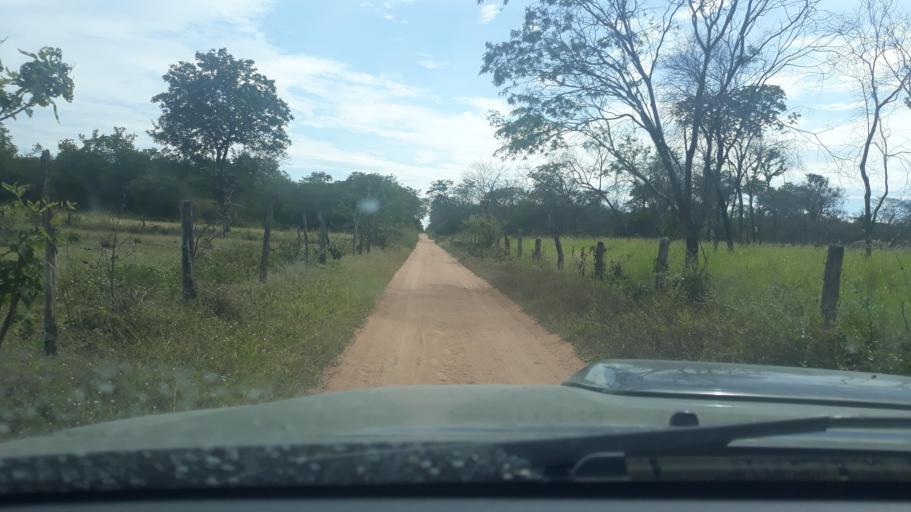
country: BR
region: Bahia
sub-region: Riacho De Santana
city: Riacho de Santana
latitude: -13.8672
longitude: -43.0183
